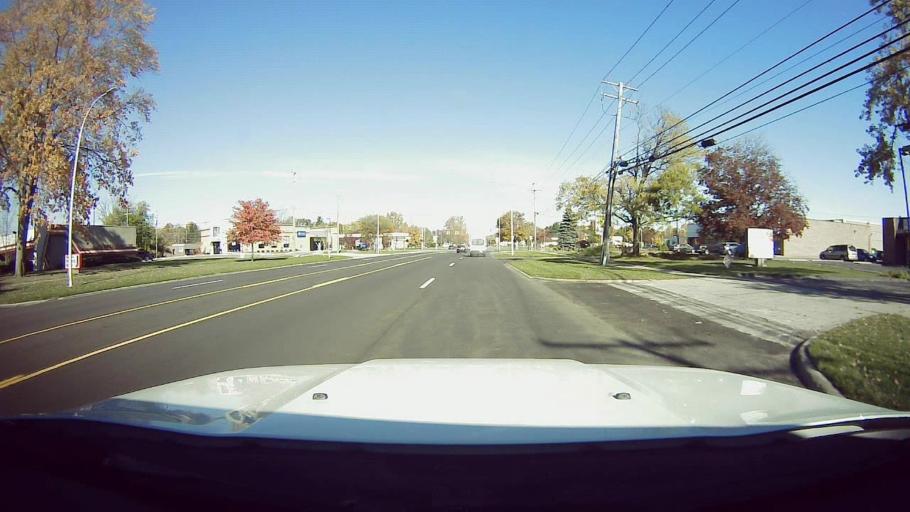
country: US
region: Michigan
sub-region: Oakland County
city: Farmington
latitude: 42.4394
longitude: -83.3754
